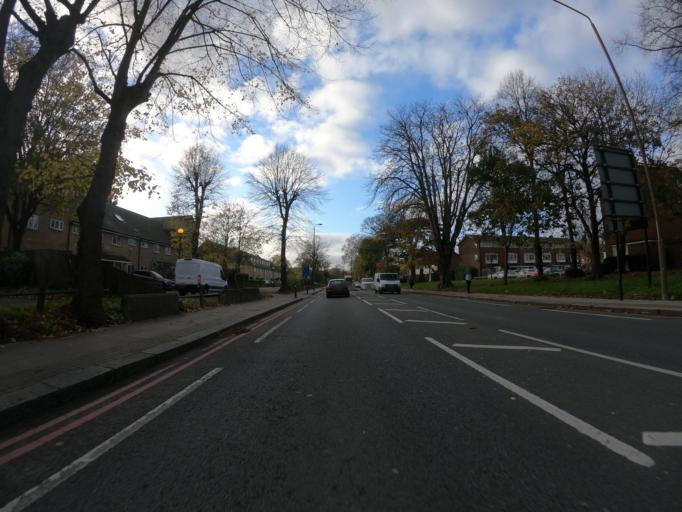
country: GB
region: England
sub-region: Greater London
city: Blackheath
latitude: 51.4539
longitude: 0.0236
